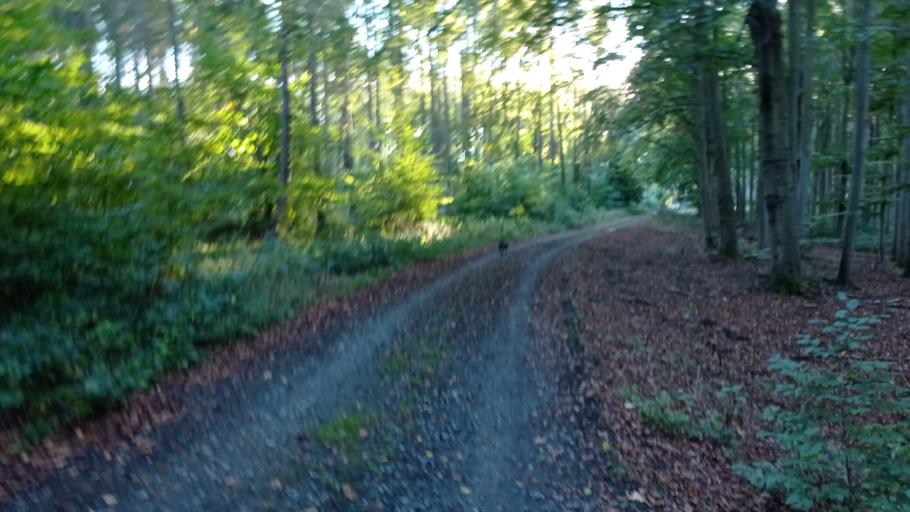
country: CZ
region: Central Bohemia
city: Chynava
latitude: 50.0546
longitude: 14.0492
